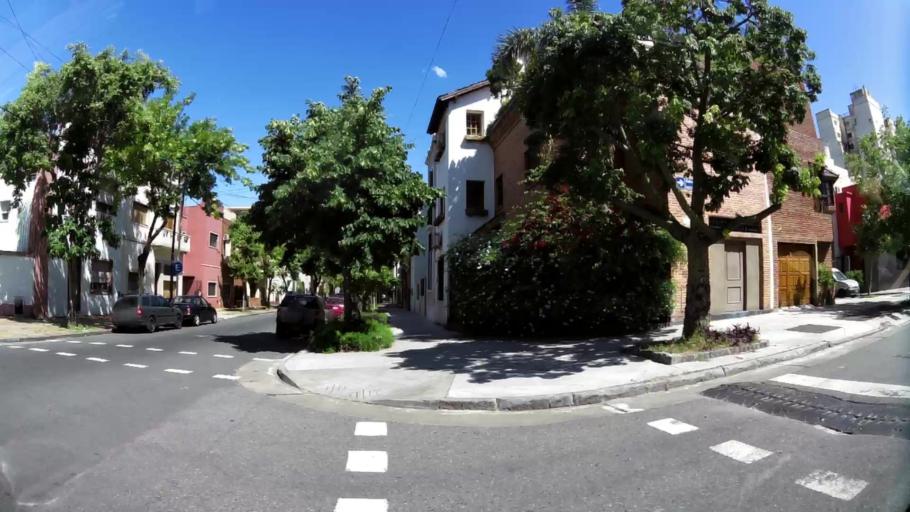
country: AR
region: Buenos Aires F.D.
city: Villa Santa Rita
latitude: -34.6330
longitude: -58.4390
